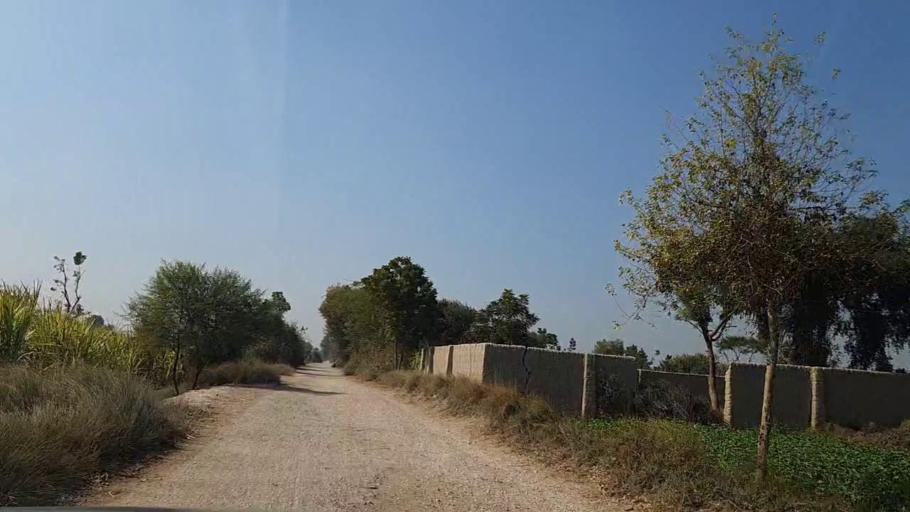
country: PK
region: Sindh
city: Daulatpur
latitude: 26.2905
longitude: 68.0675
